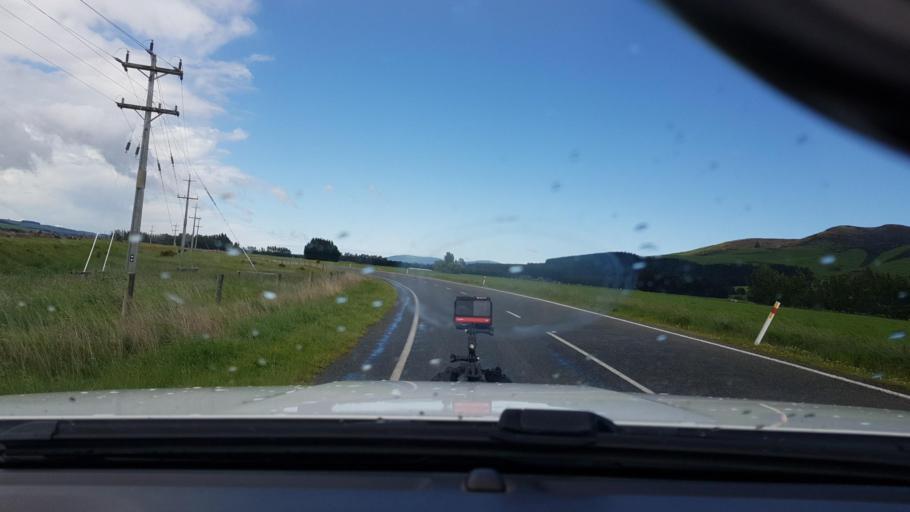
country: NZ
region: Southland
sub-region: Southland District
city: Winton
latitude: -45.7980
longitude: 168.3775
